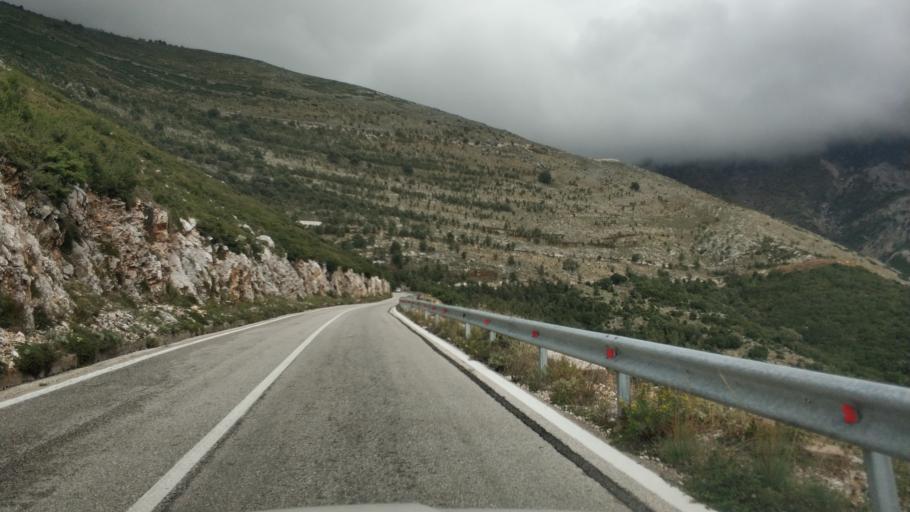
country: AL
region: Vlore
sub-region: Rrethi i Vlores
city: Vranisht
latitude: 40.1818
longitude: 19.6054
